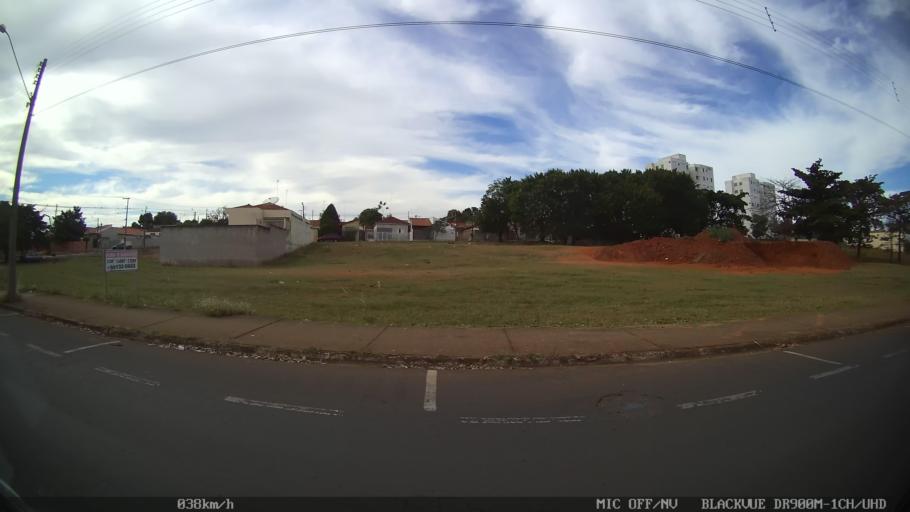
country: BR
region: Sao Paulo
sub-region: Catanduva
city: Catanduva
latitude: -21.1313
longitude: -48.9854
